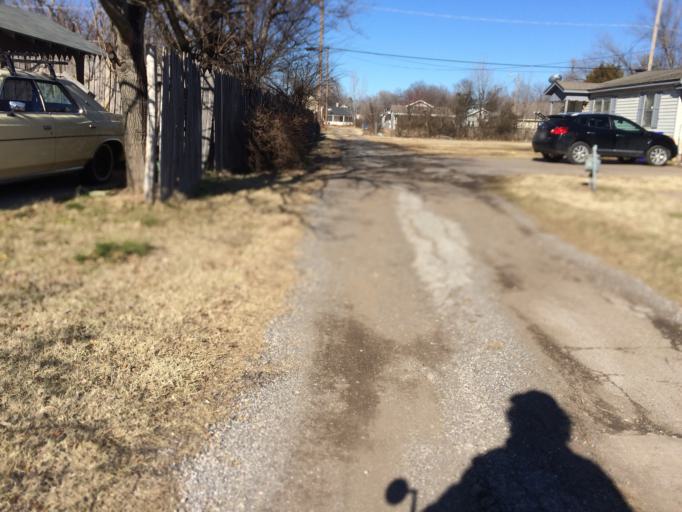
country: US
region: Oklahoma
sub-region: Cleveland County
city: Norman
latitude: 35.2221
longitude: -97.4312
